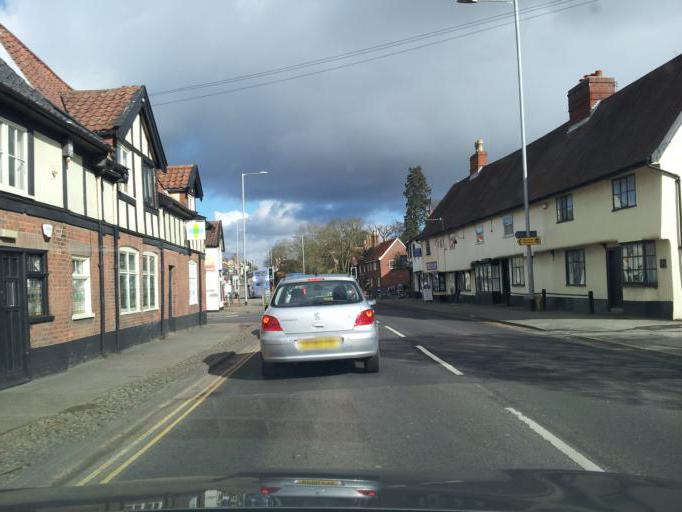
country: GB
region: England
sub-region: Norfolk
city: Long Stratton
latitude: 52.4879
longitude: 1.2346
